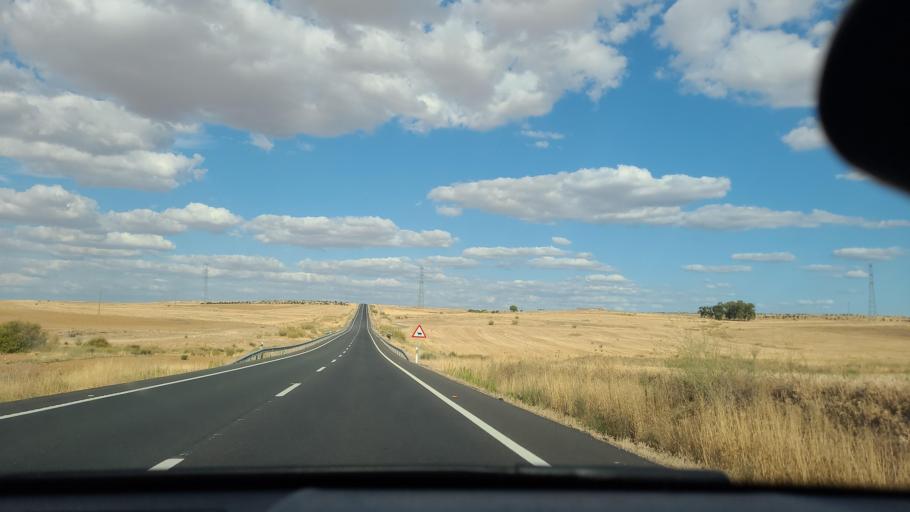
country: ES
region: Extremadura
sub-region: Provincia de Badajoz
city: Ahillones
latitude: 38.2538
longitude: -5.9147
